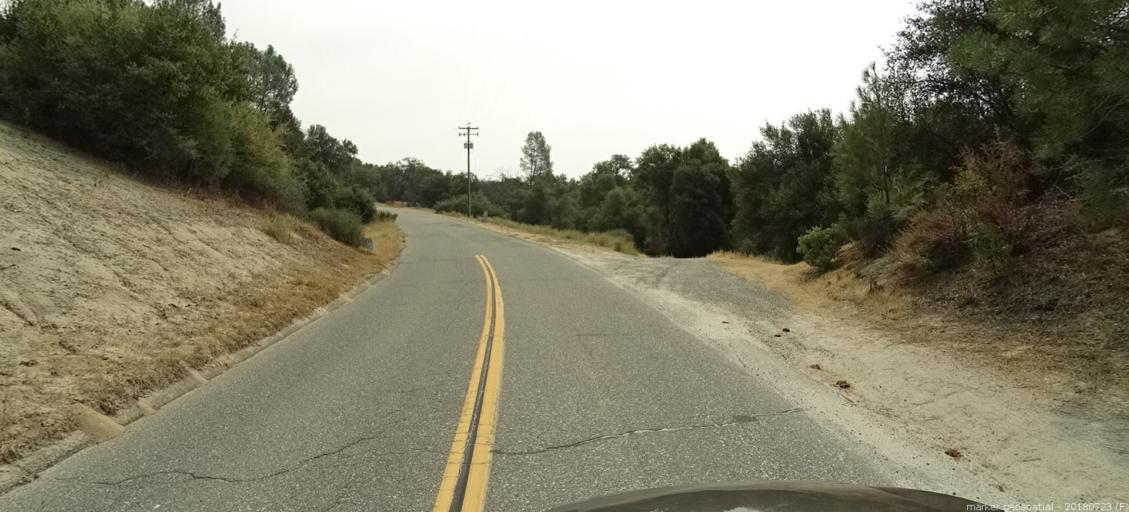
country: US
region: California
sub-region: Madera County
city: Ahwahnee
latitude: 37.3557
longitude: -119.6855
